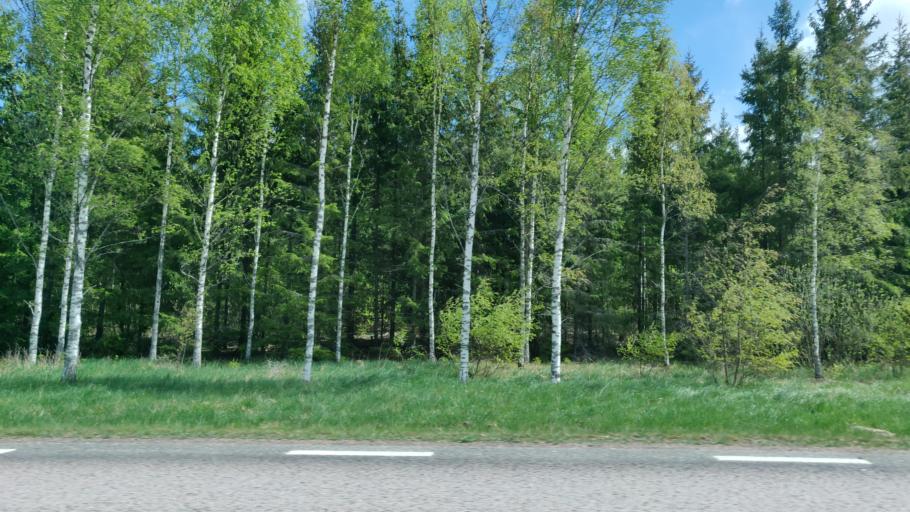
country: SE
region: Vaermland
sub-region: Karlstads Kommun
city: Skattkarr
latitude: 59.5167
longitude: 13.6169
